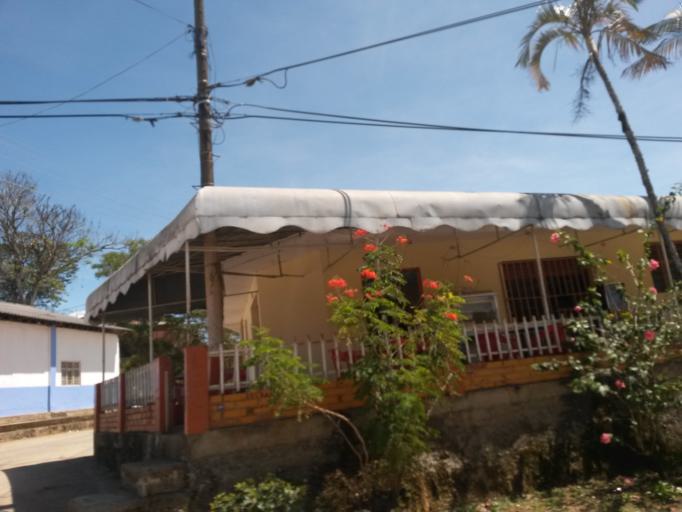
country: CO
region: Cauca
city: El Tambo
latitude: 2.4530
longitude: -76.8122
